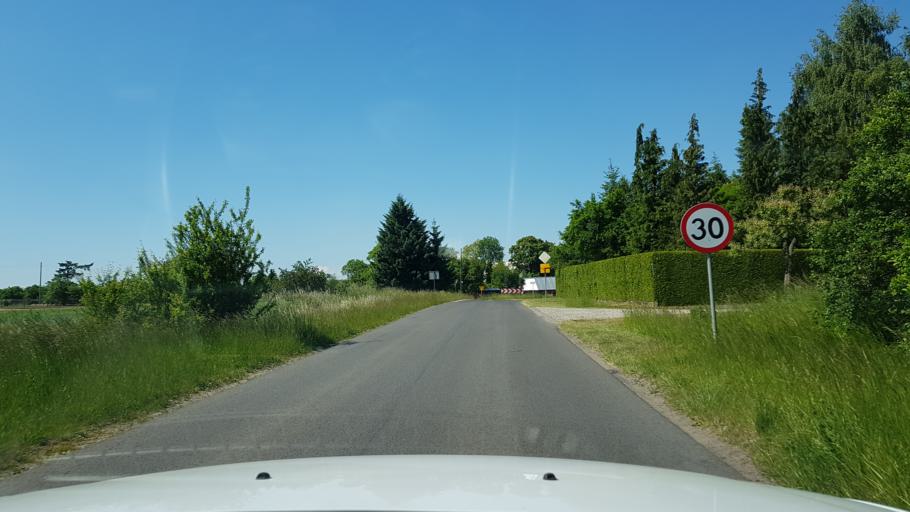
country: PL
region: West Pomeranian Voivodeship
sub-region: Powiat gryfinski
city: Banie
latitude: 53.0793
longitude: 14.6141
